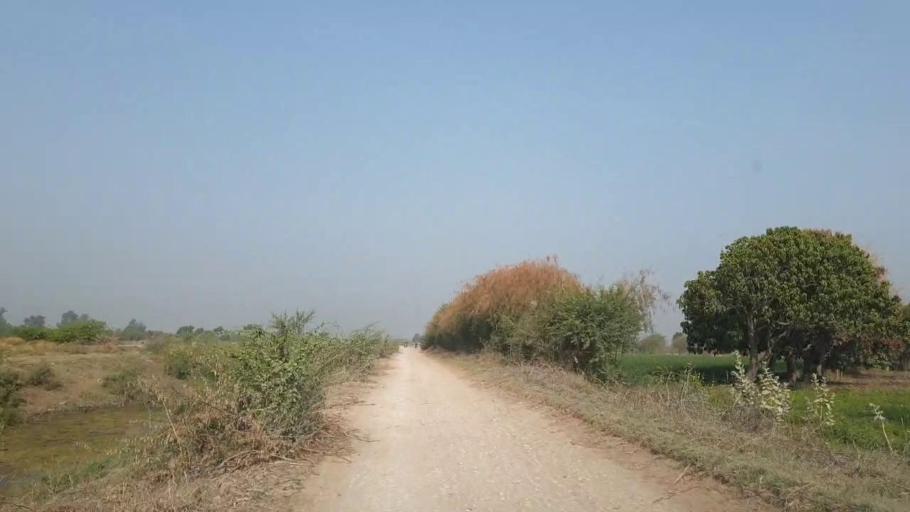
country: PK
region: Sindh
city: Mirpur Khas
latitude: 25.5560
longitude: 69.0165
